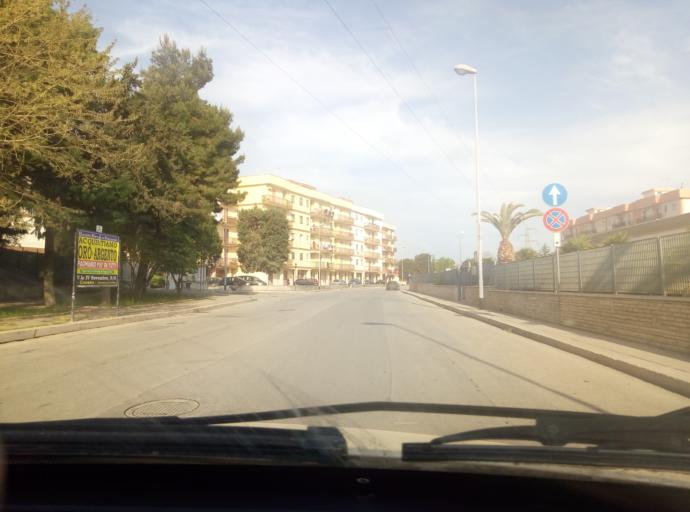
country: IT
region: Apulia
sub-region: Provincia di Bari
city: Corato
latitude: 41.1432
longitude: 16.4082
